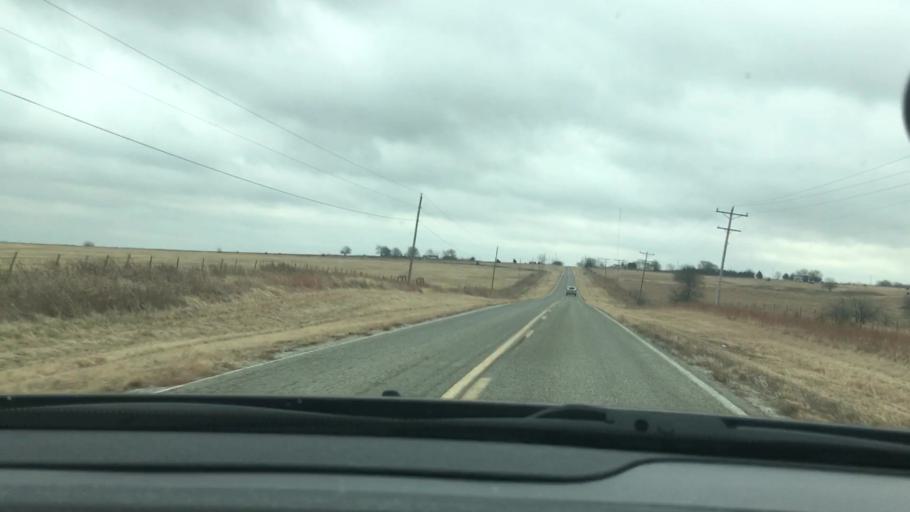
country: US
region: Oklahoma
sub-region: Johnston County
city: Tishomingo
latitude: 34.1433
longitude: -96.5119
